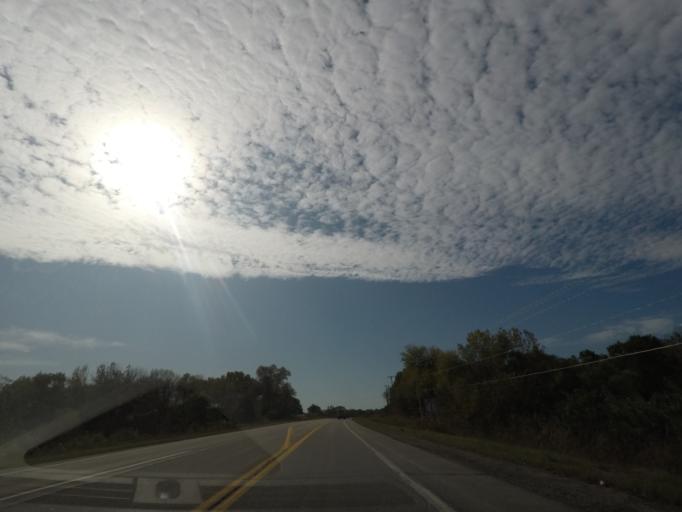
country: US
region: Iowa
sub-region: Story County
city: Gilbert
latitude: 42.0772
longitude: -93.6209
